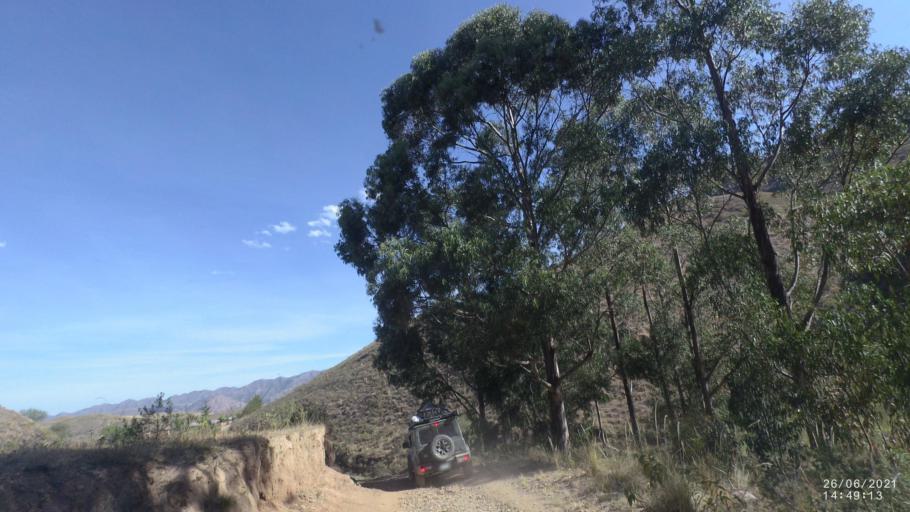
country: BO
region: Cochabamba
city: Mizque
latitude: -17.9201
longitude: -65.6256
